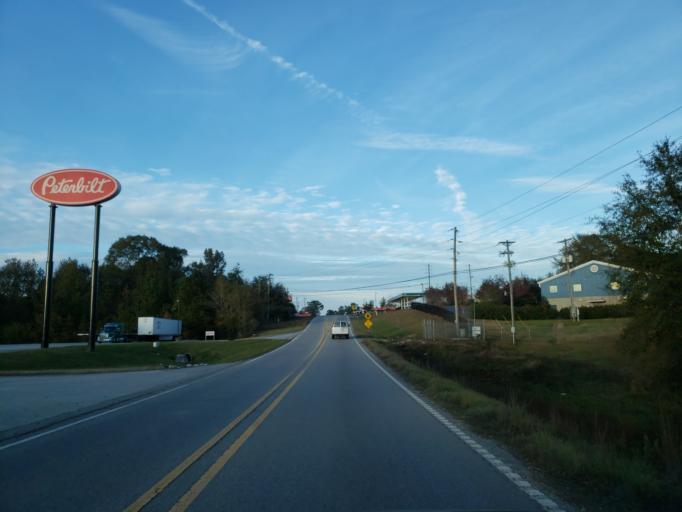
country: US
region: Mississippi
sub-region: Lamar County
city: West Hattiesburg
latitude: 31.2541
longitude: -89.3403
